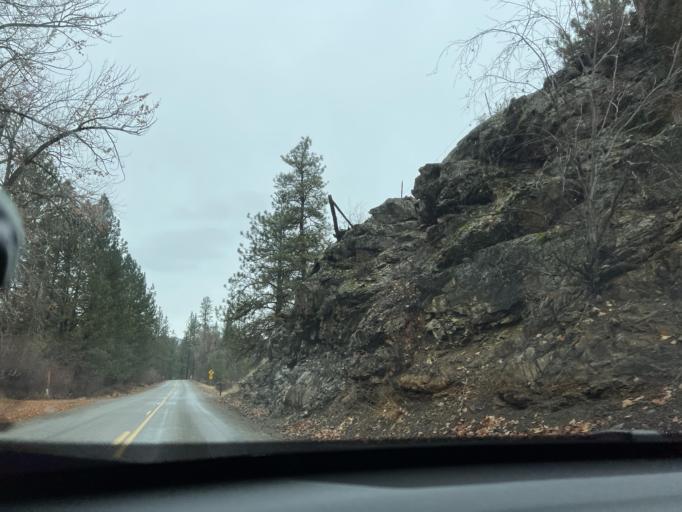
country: US
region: Washington
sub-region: Okanogan County
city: Brewster
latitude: 48.5272
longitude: -120.1798
